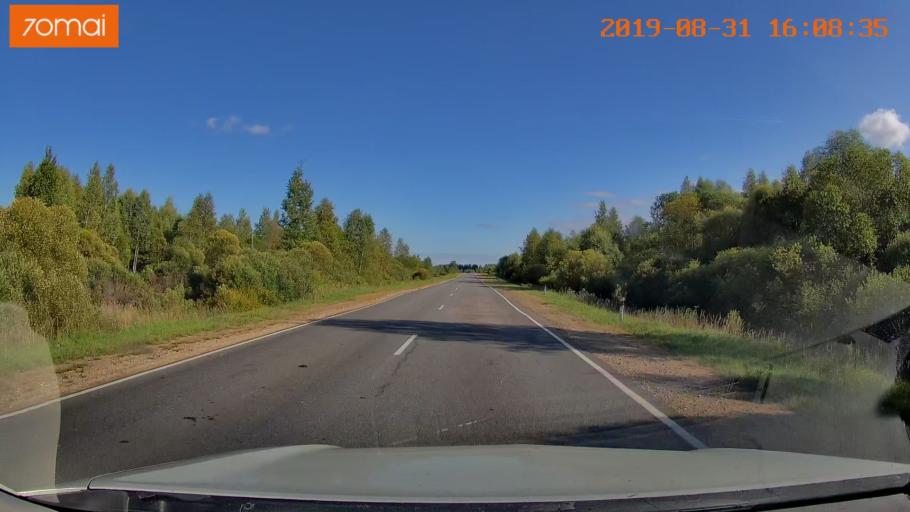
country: RU
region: Kaluga
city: Yukhnov
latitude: 54.5951
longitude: 35.3784
